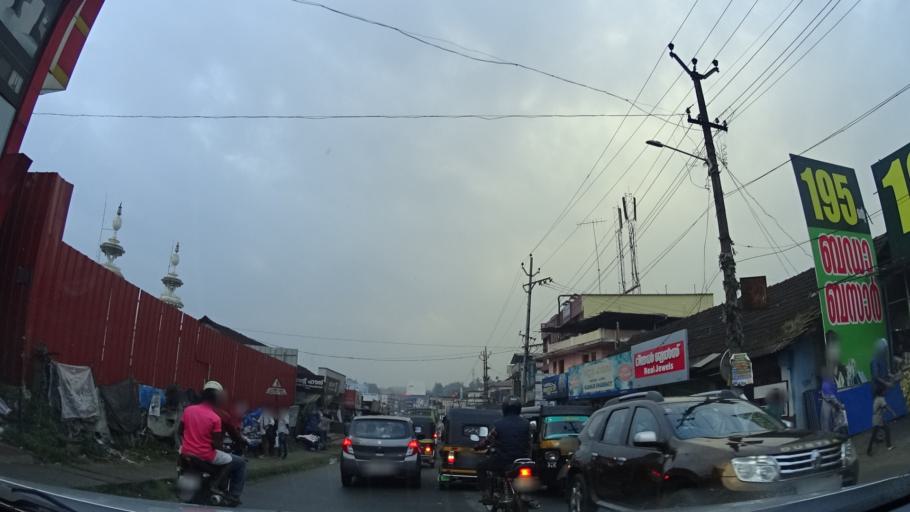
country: IN
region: Kerala
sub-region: Wayanad
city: Kalpetta
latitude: 11.6110
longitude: 76.0828
